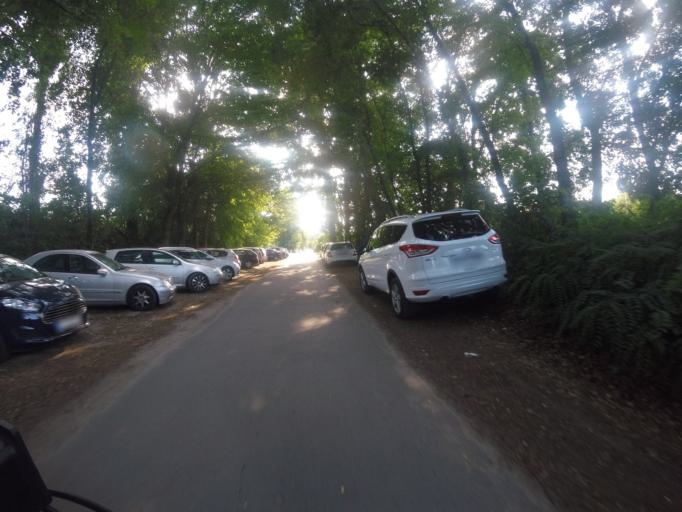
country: DE
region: Berlin
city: Westend
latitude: 52.5286
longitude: 13.2781
